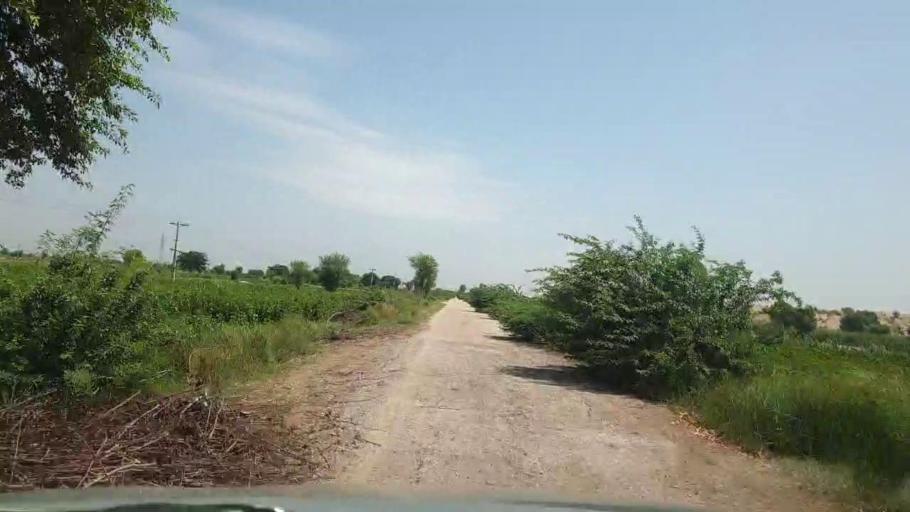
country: PK
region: Sindh
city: Bozdar
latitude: 27.0962
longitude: 68.9725
